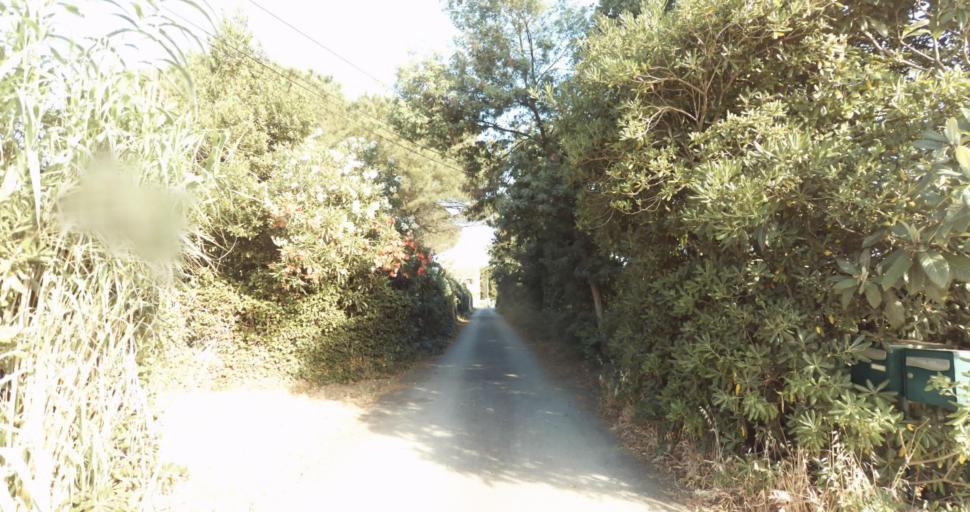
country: FR
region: Provence-Alpes-Cote d'Azur
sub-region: Departement du Var
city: Saint-Tropez
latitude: 43.2570
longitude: 6.6313
